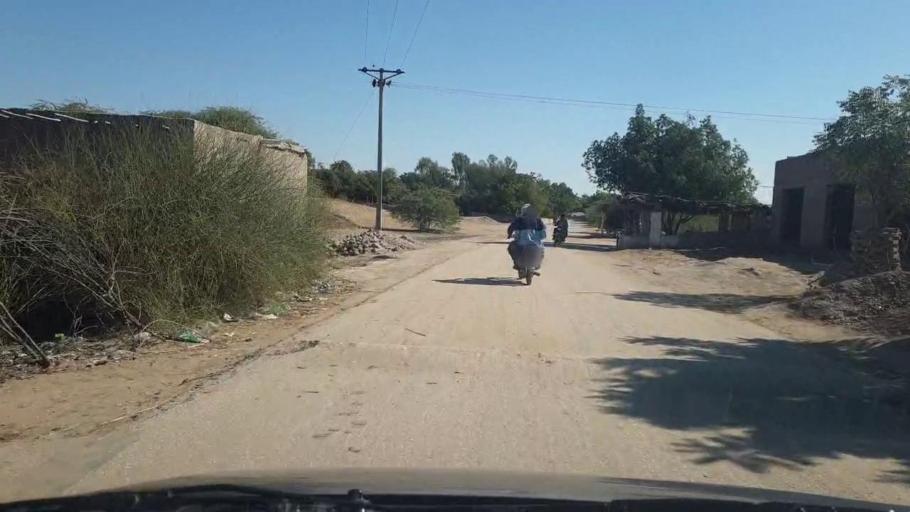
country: PK
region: Sindh
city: Bozdar
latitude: 27.0594
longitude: 68.6385
